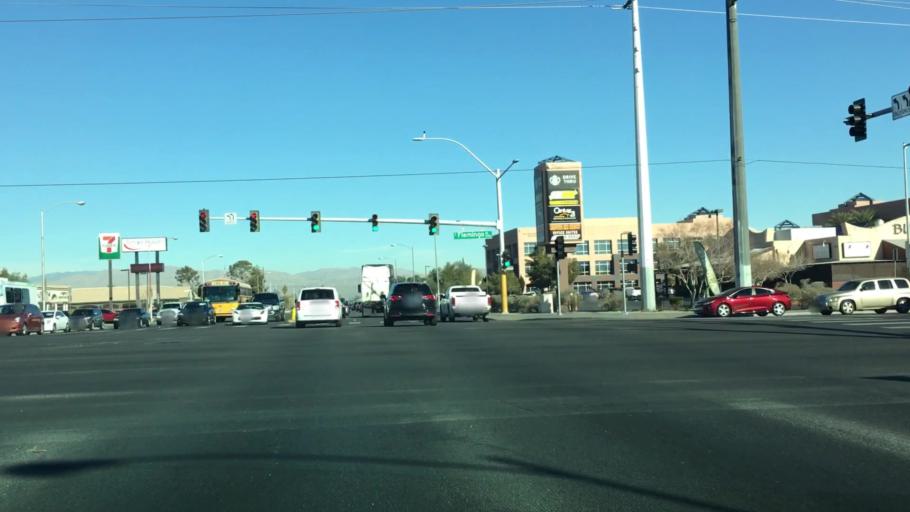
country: US
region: Nevada
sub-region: Clark County
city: Winchester
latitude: 36.1145
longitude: -115.1191
